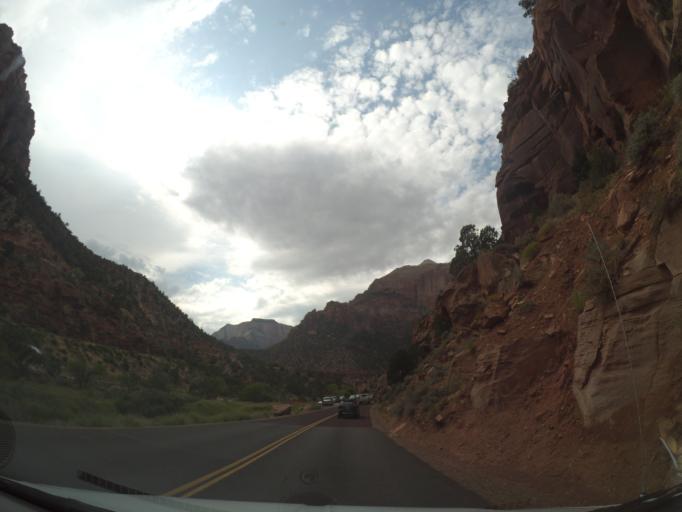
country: US
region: Utah
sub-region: Washington County
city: Hildale
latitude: 37.2167
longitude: -112.9672
